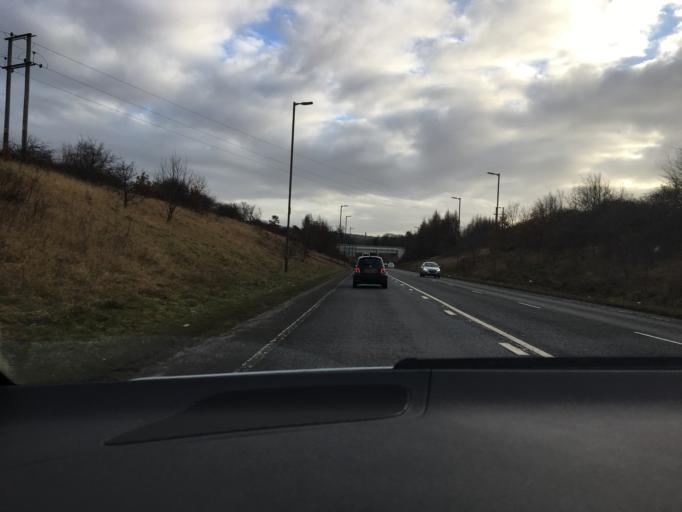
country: GB
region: Scotland
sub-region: Midlothian
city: Bonnyrigg
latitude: 55.8794
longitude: -3.0858
